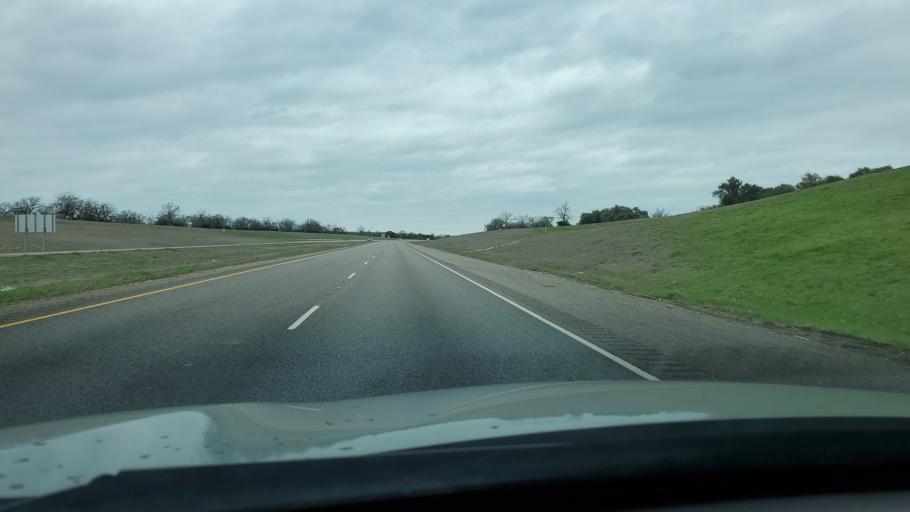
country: US
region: Texas
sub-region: Williamson County
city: Florence
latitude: 30.8558
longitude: -97.7930
